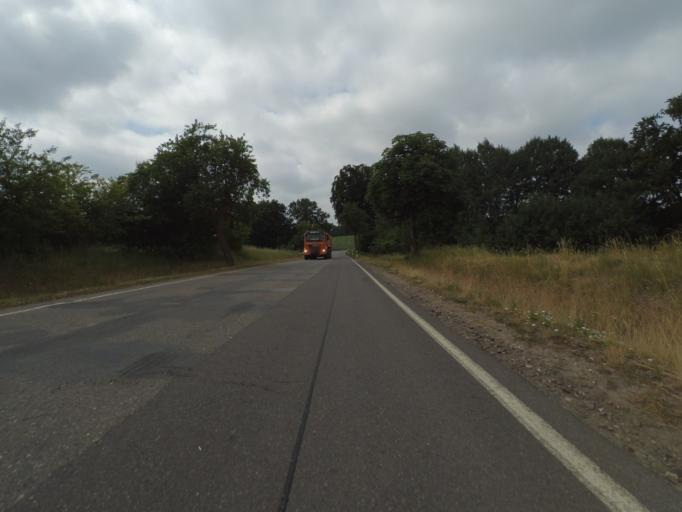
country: DE
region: Mecklenburg-Vorpommern
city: Krakow am See
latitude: 53.6225
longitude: 12.3354
